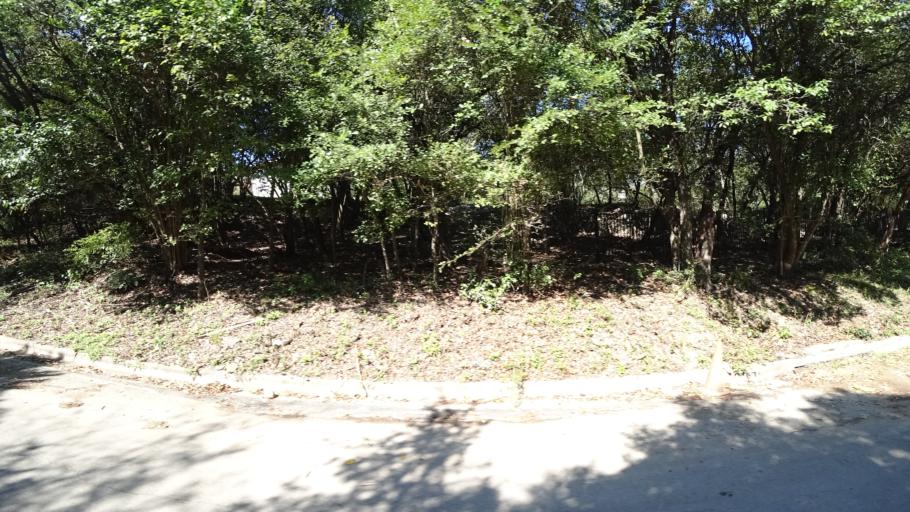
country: US
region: Texas
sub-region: Travis County
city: Rollingwood
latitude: 30.2770
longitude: -97.8021
